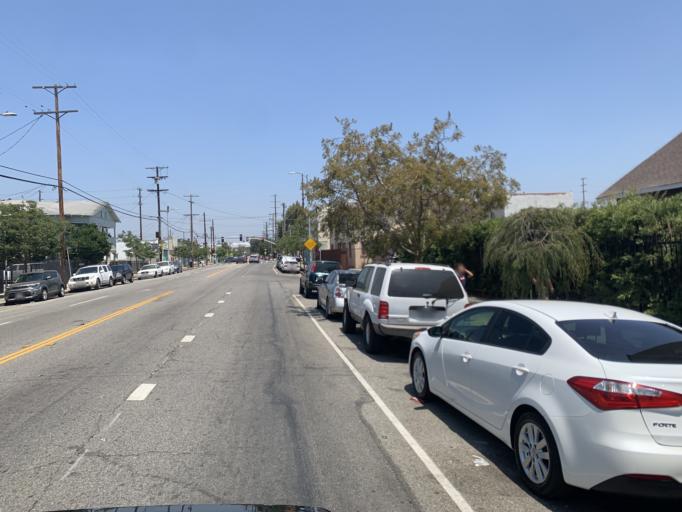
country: US
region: California
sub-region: Los Angeles County
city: Florence-Graham
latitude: 34.0024
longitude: -118.2871
